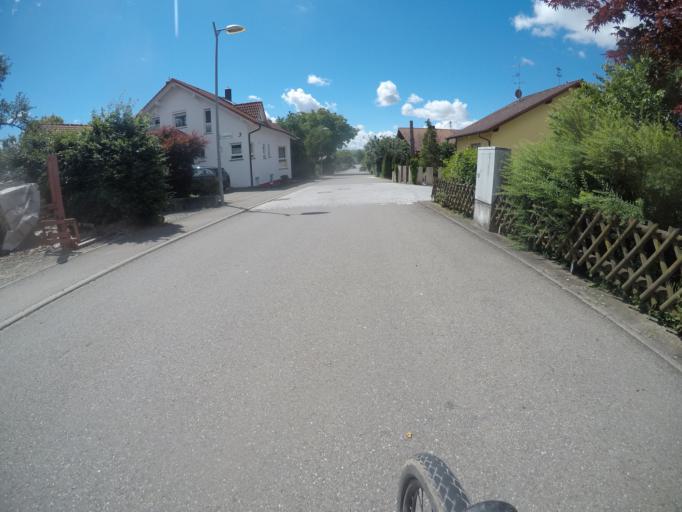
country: DE
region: Baden-Wuerttemberg
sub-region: Karlsruhe Region
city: Horb am Neckar
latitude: 48.4773
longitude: 8.7451
